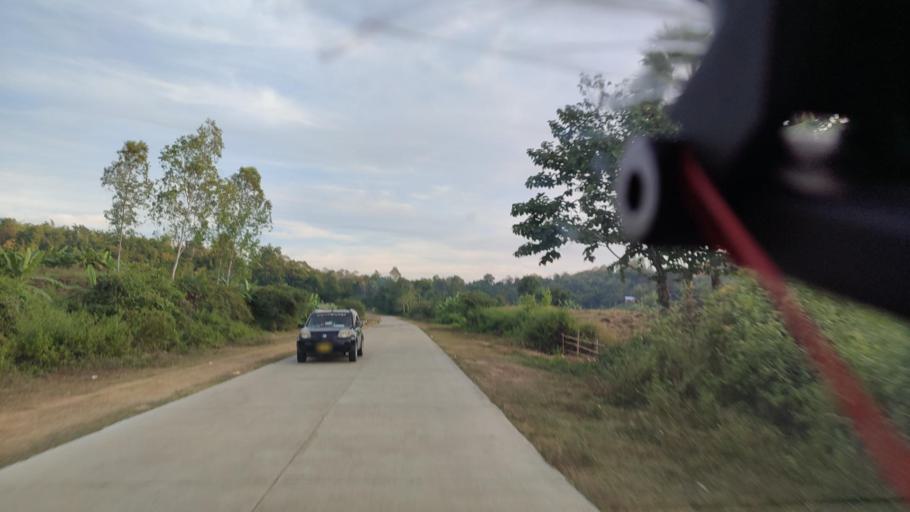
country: MM
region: Mandalay
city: Nay Pyi Taw
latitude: 19.9326
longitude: 95.9790
